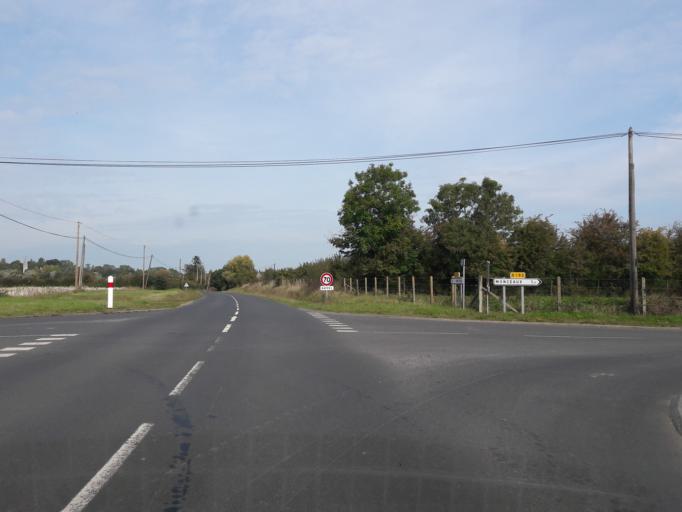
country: FR
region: Lower Normandy
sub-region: Departement du Calvados
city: Bayeux
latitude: 49.2394
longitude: -0.7035
